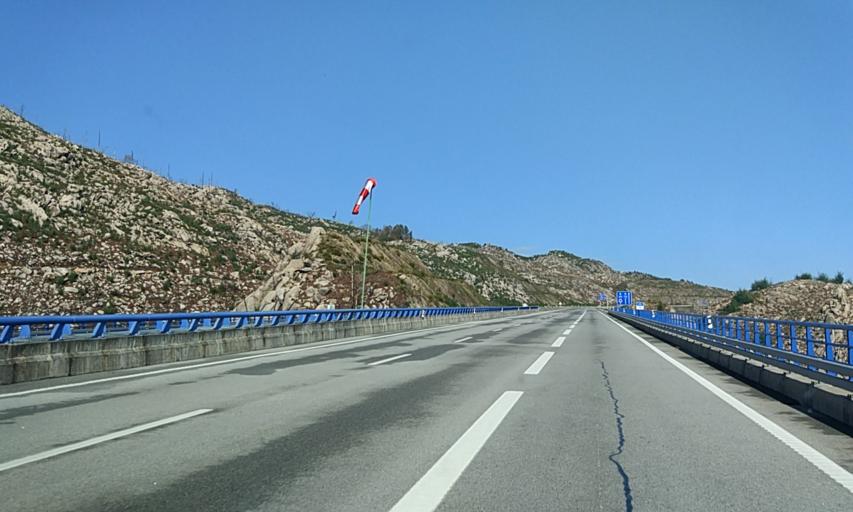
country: PT
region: Viseu
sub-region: Vouzela
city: Vouzela
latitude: 40.6665
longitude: -8.0748
